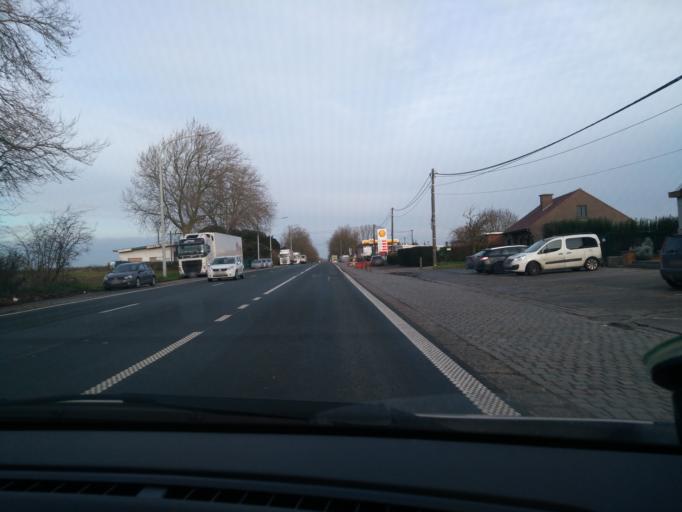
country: BE
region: Wallonia
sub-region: Province du Hainaut
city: Quevy-le-Petit
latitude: 50.3442
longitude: 3.9704
